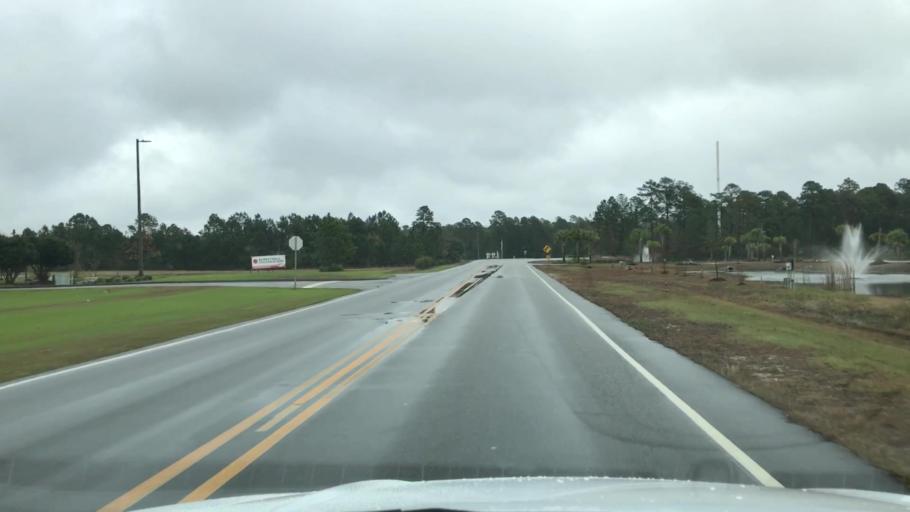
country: US
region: South Carolina
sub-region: Horry County
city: Forestbrook
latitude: 33.7598
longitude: -78.9219
